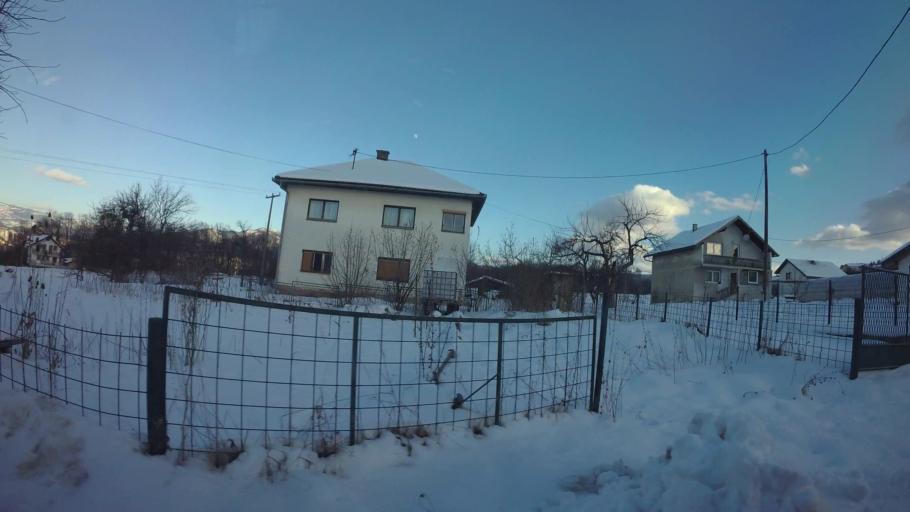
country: BA
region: Federation of Bosnia and Herzegovina
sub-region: Kanton Sarajevo
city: Sarajevo
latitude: 43.8093
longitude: 18.3561
